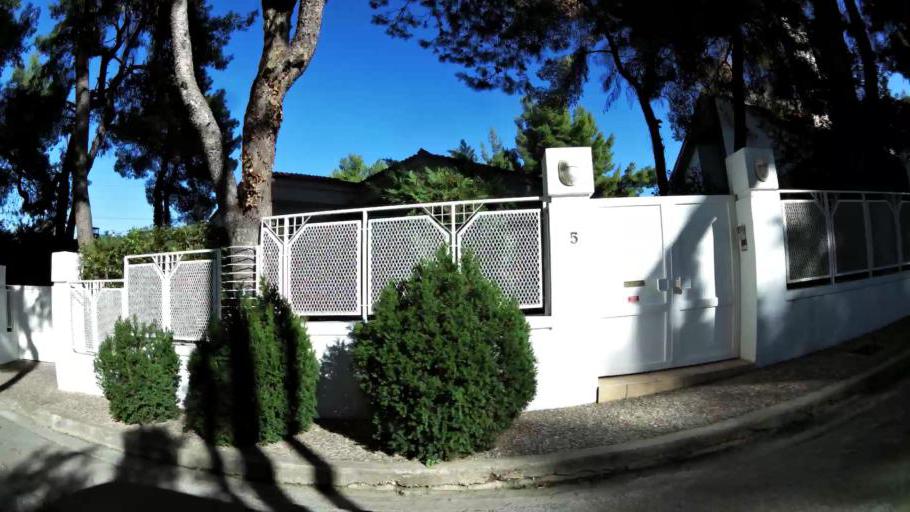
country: GR
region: Attica
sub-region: Nomarchia Anatolikis Attikis
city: Drosia
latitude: 38.1149
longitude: 23.8561
